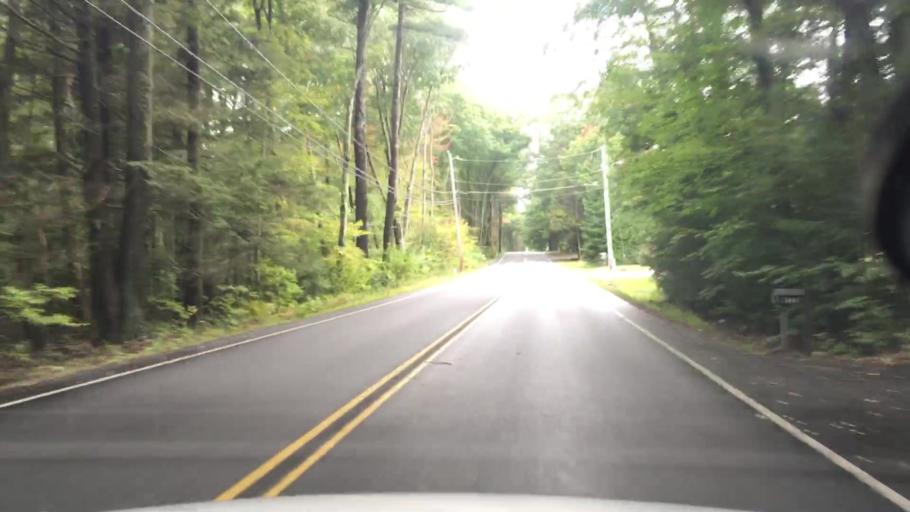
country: US
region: New Hampshire
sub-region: Strafford County
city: Rochester
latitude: 43.2836
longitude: -70.9563
